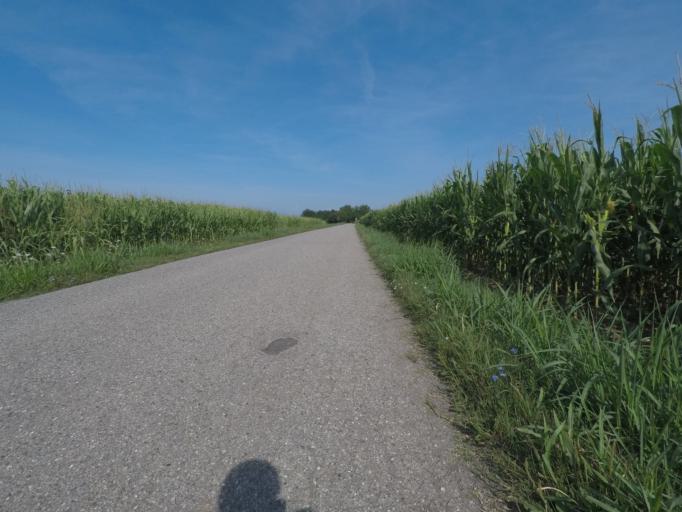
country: IT
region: Friuli Venezia Giulia
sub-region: Provincia di Udine
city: Basiliano-Vissandone
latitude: 46.0628
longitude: 13.1022
